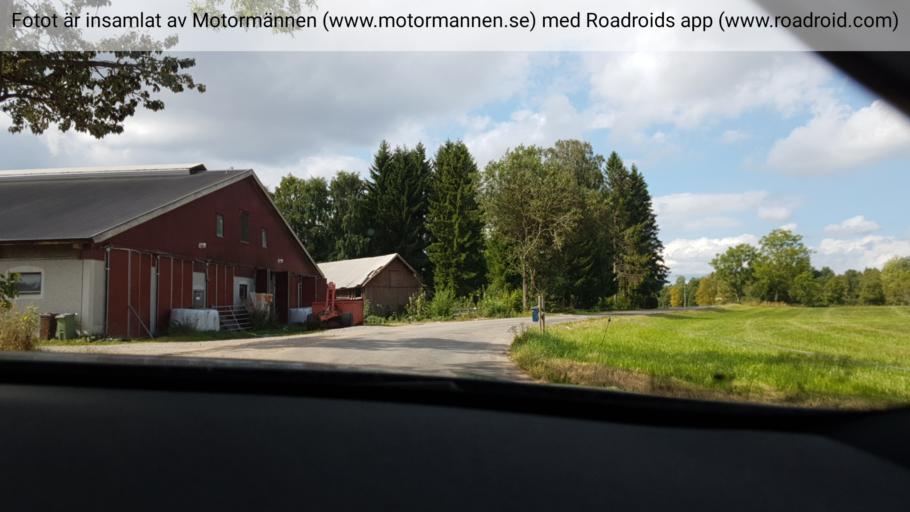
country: SE
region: Vaestra Goetaland
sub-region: Falkopings Kommun
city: Floby
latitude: 57.9964
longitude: 13.3000
